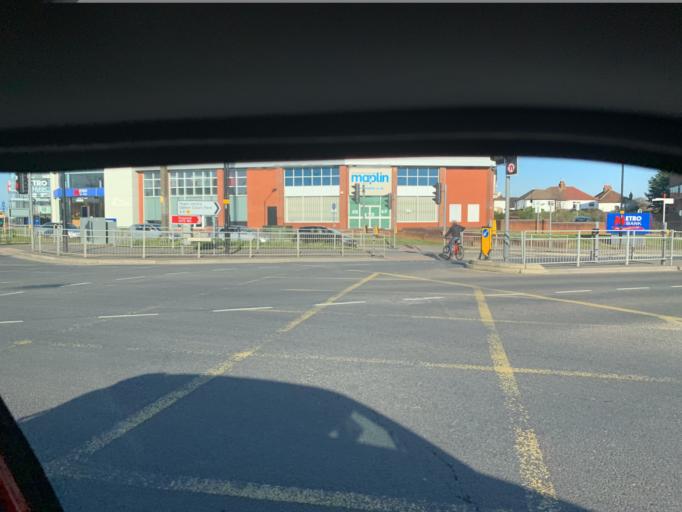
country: GB
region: England
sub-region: Slough
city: Slough
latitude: 51.5125
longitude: -0.6124
